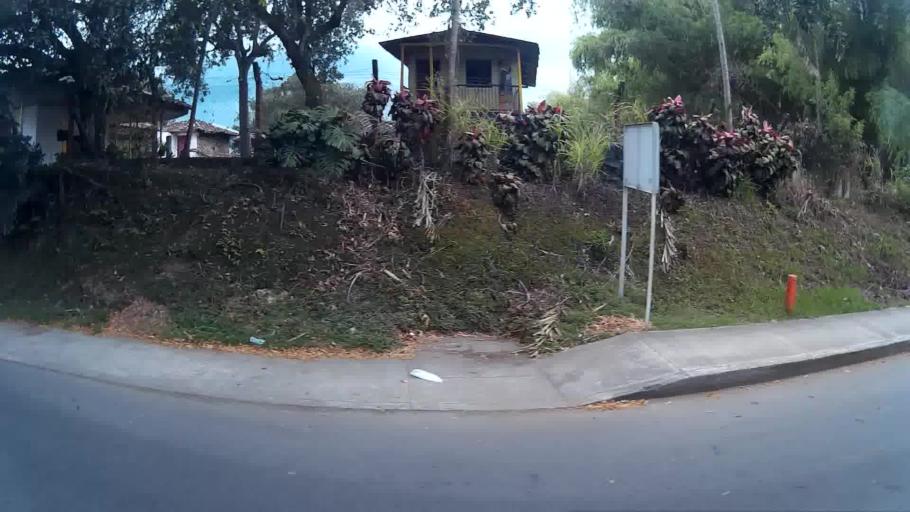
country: CO
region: Risaralda
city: Pereira
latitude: 4.8136
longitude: -75.7834
